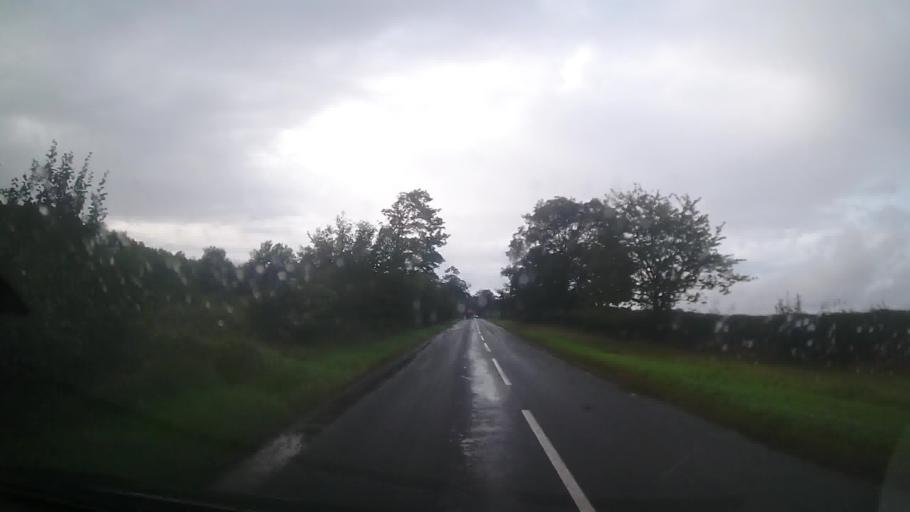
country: GB
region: England
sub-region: Oxfordshire
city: Stonesfield
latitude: 51.8706
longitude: -1.4136
